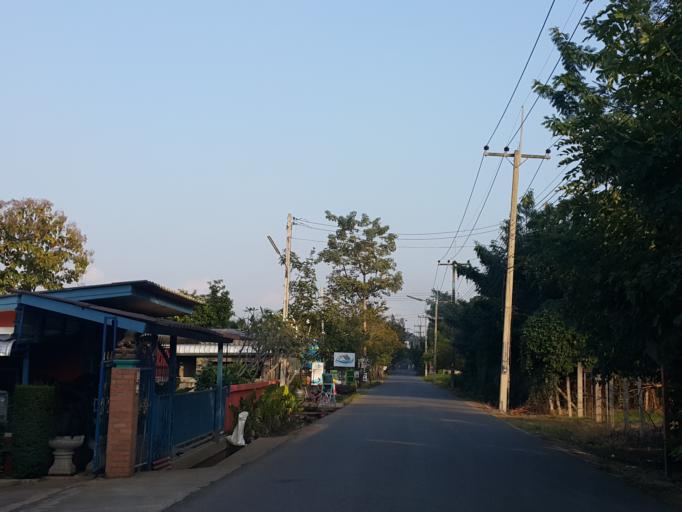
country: TH
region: Chiang Mai
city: Chiang Mai
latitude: 18.9086
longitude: 98.9081
